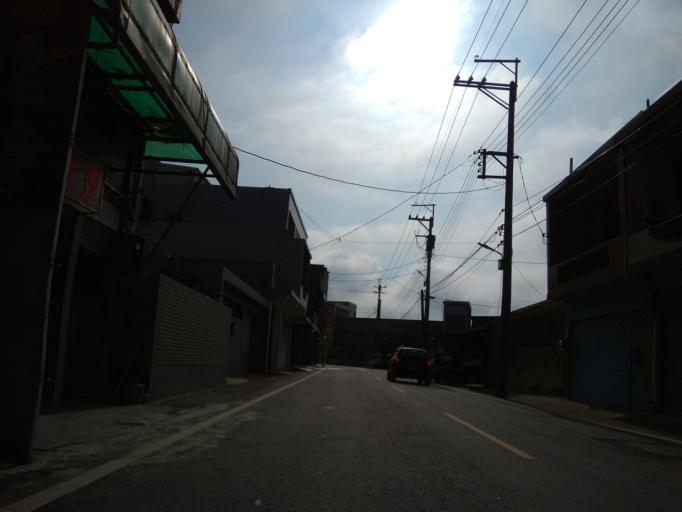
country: TW
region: Taiwan
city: Taoyuan City
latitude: 25.0771
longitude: 121.1698
